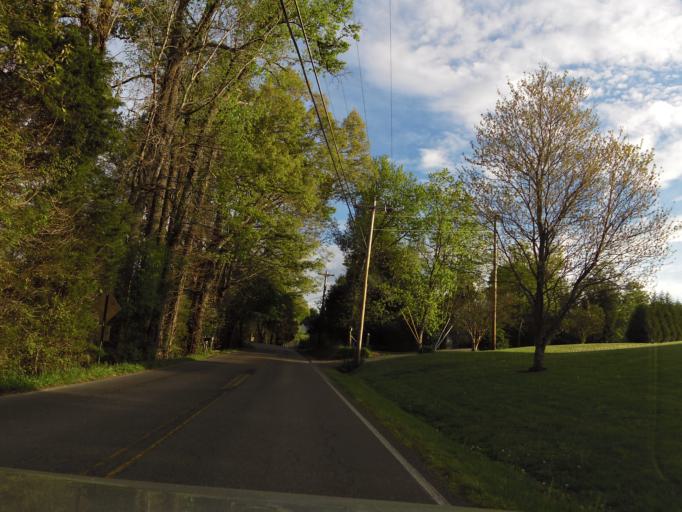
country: US
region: Tennessee
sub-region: Blount County
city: Maryville
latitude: 35.6666
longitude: -84.0200
